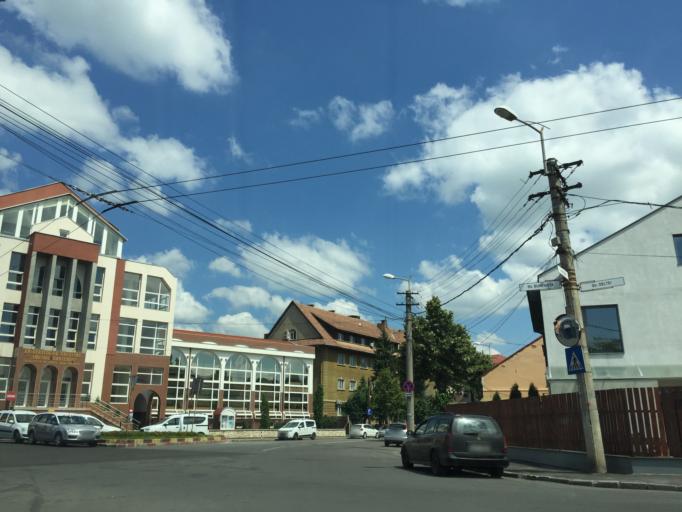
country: RO
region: Cluj
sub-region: Municipiul Cluj-Napoca
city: Cluj-Napoca
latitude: 46.7825
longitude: 23.5907
